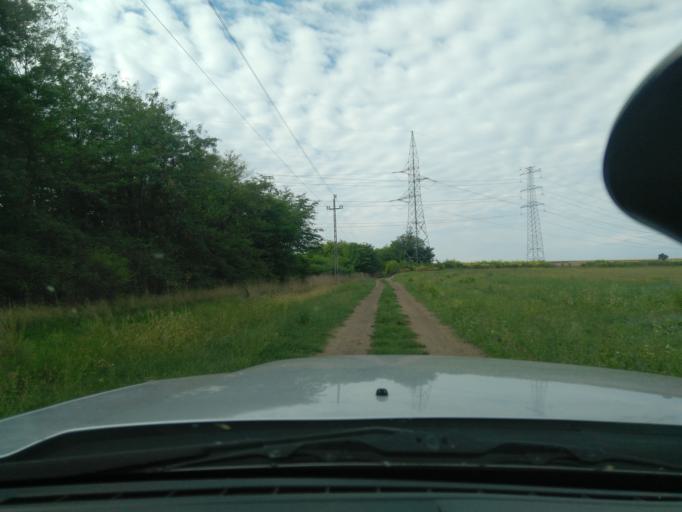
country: HU
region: Fejer
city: Val
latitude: 47.3693
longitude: 18.7106
